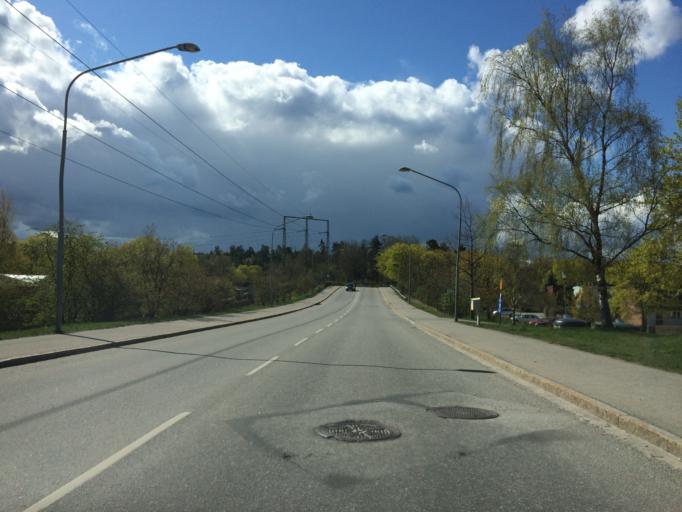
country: SE
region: Stockholm
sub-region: Huddinge Kommun
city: Segeltorp
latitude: 59.2920
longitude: 17.9237
